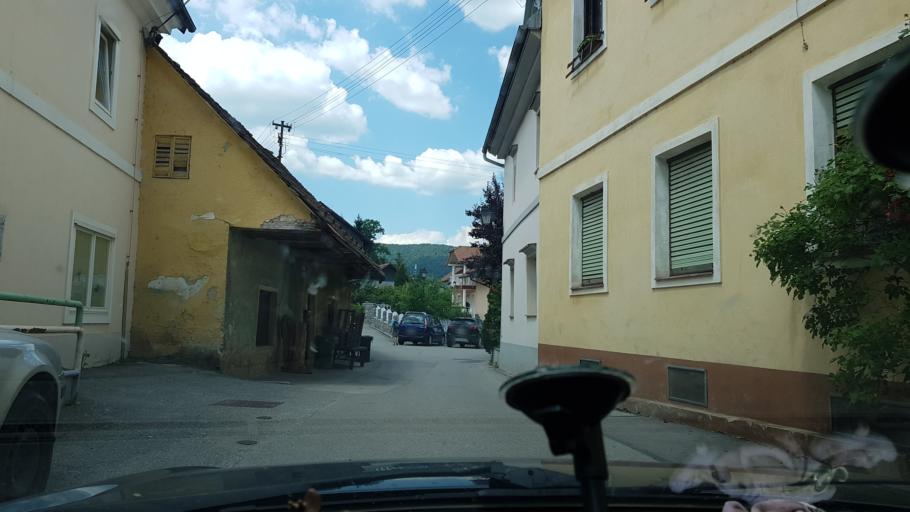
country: SI
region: Vrhnika
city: Vrhnika
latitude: 45.9609
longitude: 14.2894
